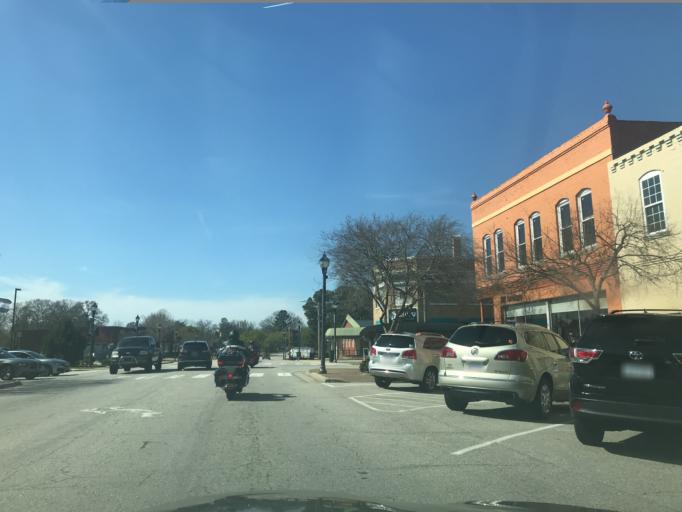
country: US
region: North Carolina
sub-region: Wake County
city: Fuquay-Varina
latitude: 35.5934
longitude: -78.7944
